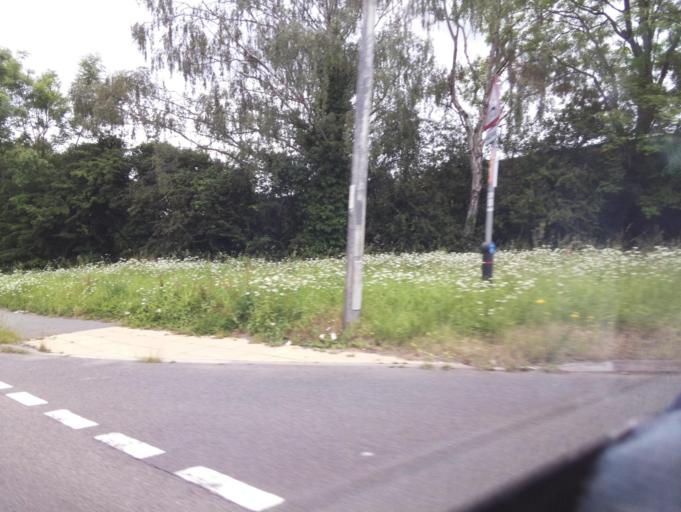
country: GB
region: England
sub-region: Staffordshire
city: Featherstone
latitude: 52.6449
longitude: -2.1272
